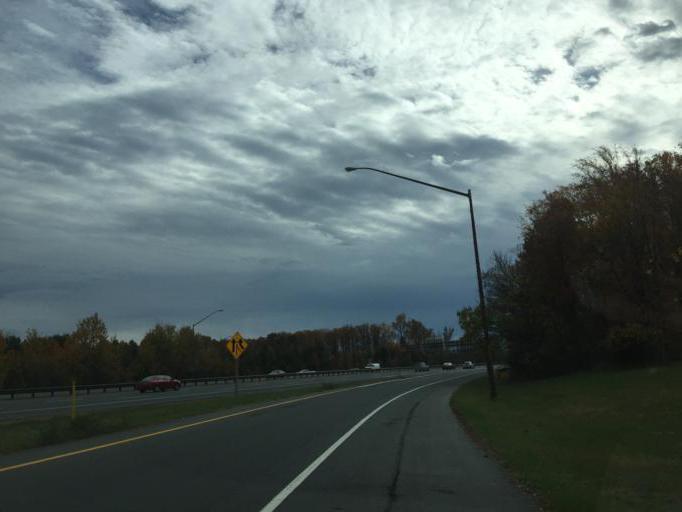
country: US
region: Maryland
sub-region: Montgomery County
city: Germantown
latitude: 39.1955
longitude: -77.2622
